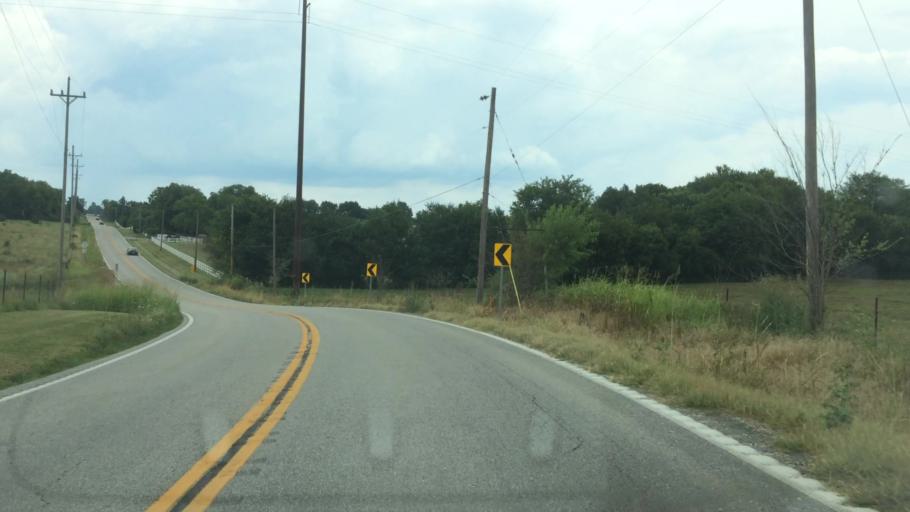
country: US
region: Missouri
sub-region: Greene County
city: Strafford
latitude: 37.2539
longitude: -93.1354
